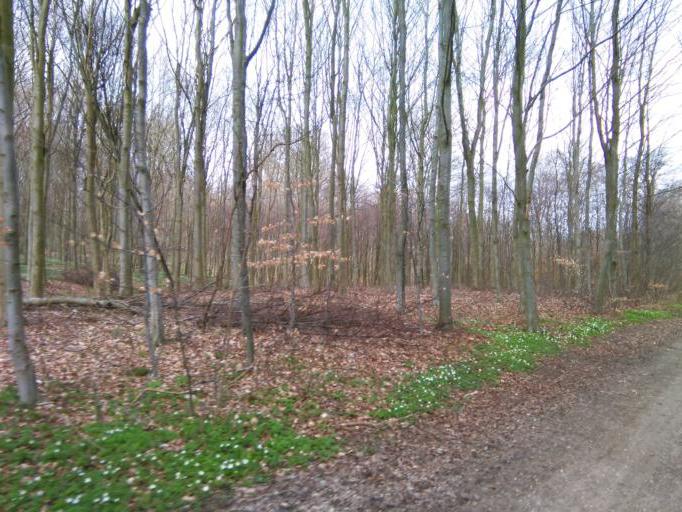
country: DK
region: Central Jutland
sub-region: Arhus Kommune
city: Beder
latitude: 56.0799
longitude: 10.2512
